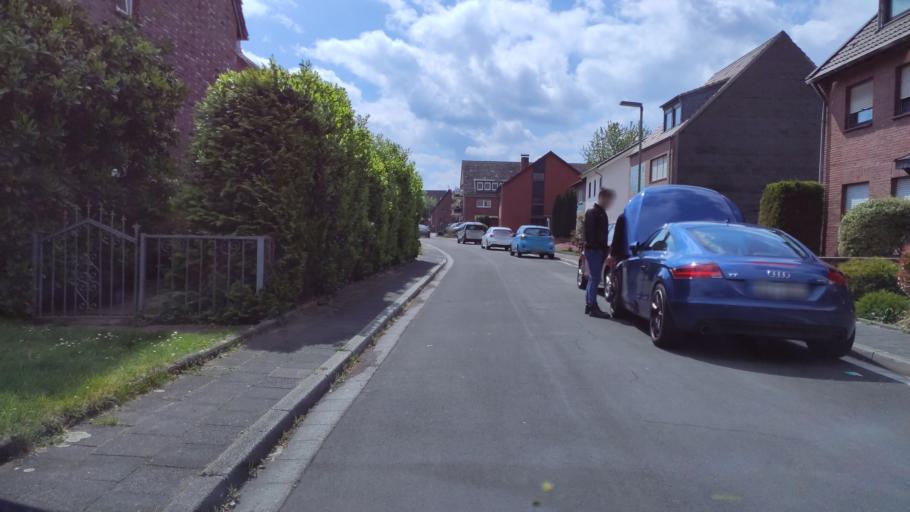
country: DE
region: North Rhine-Westphalia
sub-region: Regierungsbezirk Dusseldorf
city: Neuss
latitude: 51.1605
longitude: 6.6725
